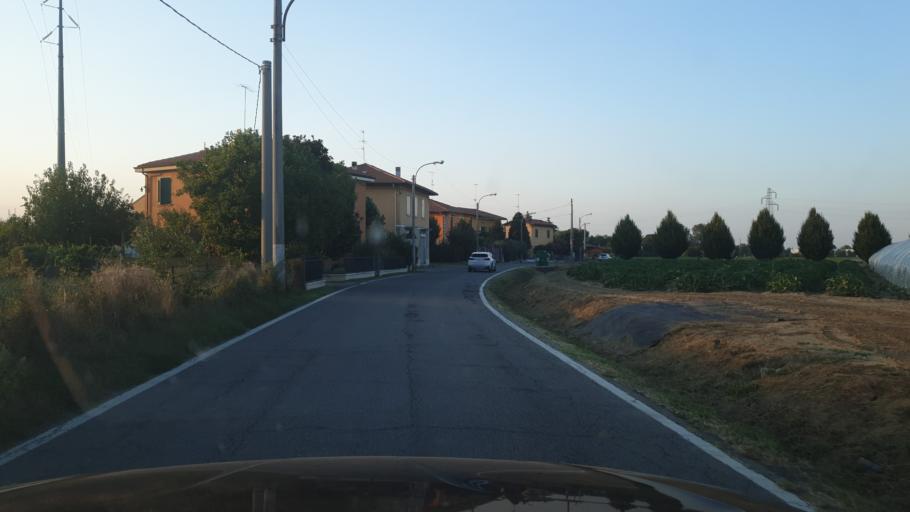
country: IT
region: Emilia-Romagna
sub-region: Provincia di Bologna
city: Quarto Inferiore
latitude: 44.5207
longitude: 11.3810
